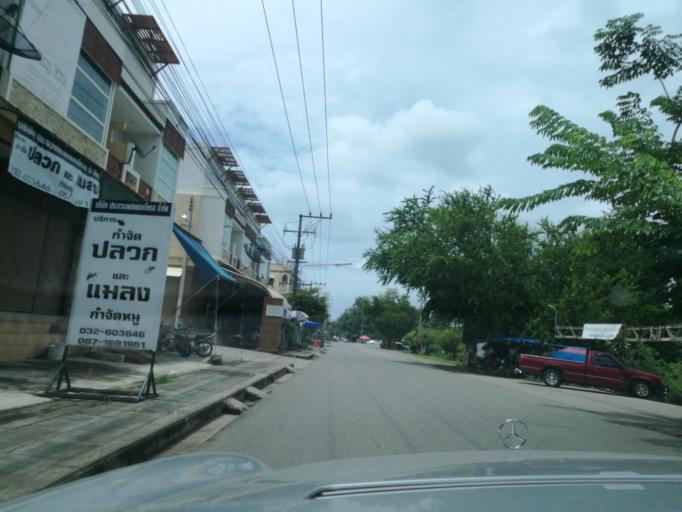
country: TH
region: Prachuap Khiri Khan
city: Prachuap Khiri Khan
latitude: 11.8131
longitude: 99.7922
